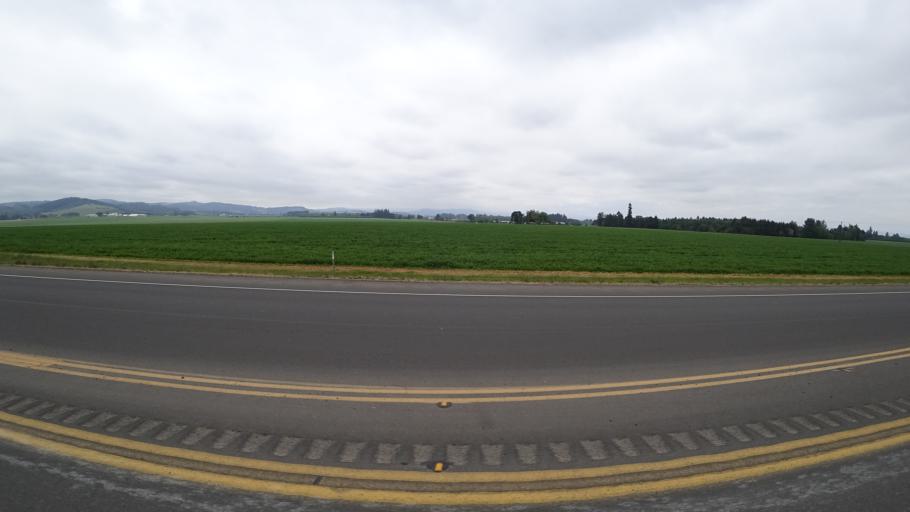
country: US
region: Oregon
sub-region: Washington County
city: Hillsboro
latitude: 45.4818
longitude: -122.9915
